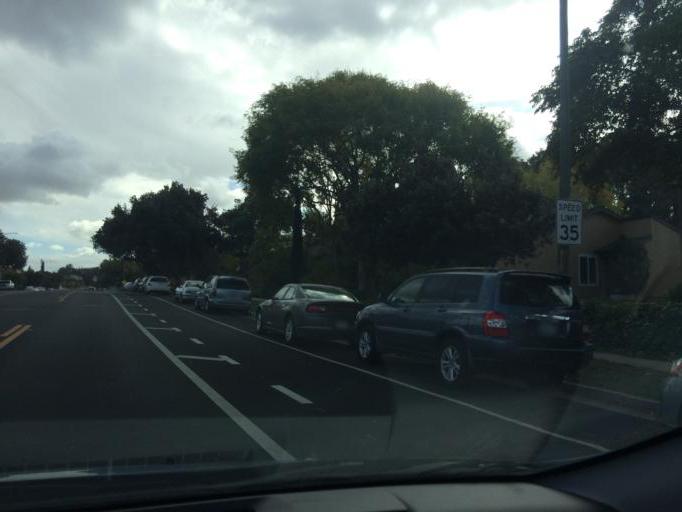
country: US
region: California
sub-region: Santa Clara County
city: Seven Trees
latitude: 37.3083
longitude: -121.7991
